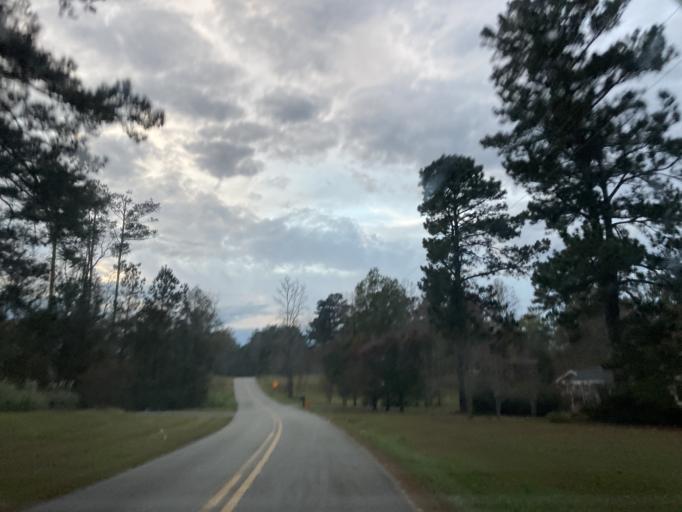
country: US
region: Georgia
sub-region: Jones County
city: Gray
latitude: 32.9778
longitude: -83.5195
